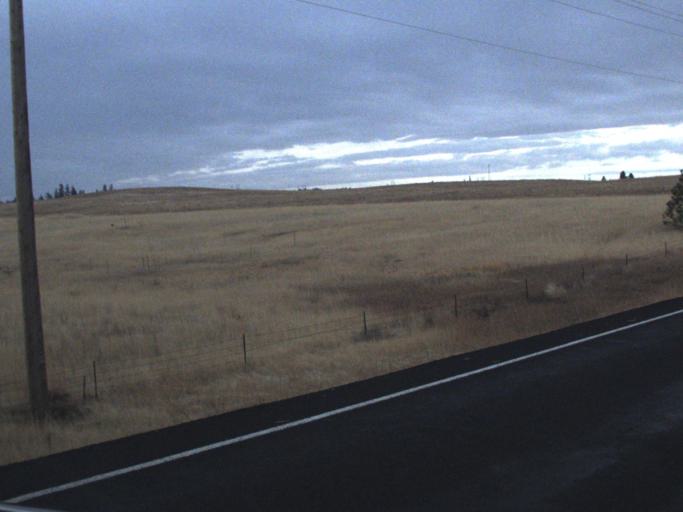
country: US
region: Washington
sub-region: Lincoln County
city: Davenport
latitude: 47.7547
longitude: -118.1734
